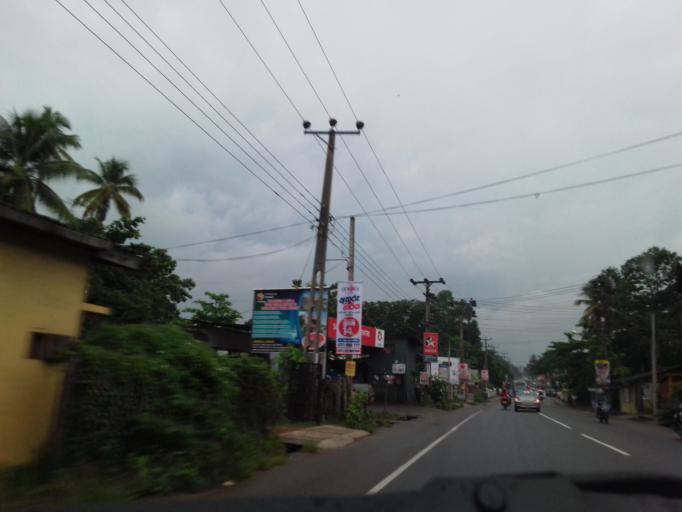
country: LK
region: Western
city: Battaramulla South
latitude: 6.8934
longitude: 79.9624
